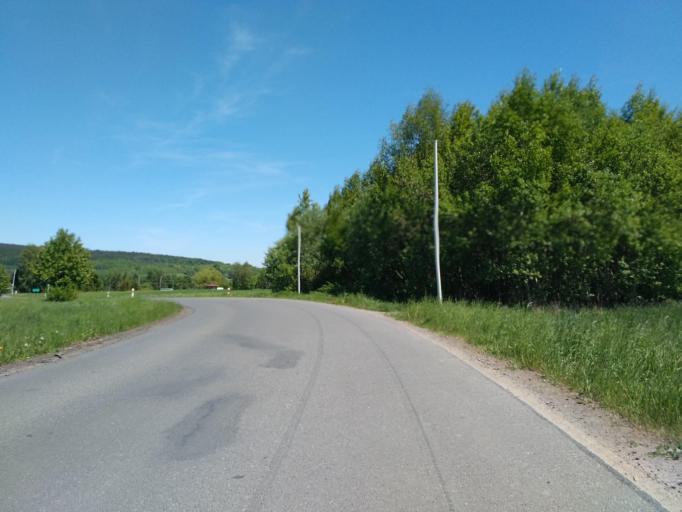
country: PL
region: Subcarpathian Voivodeship
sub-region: Powiat sanocki
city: Nowosielce-Gniewosz
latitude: 49.5517
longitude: 22.0916
